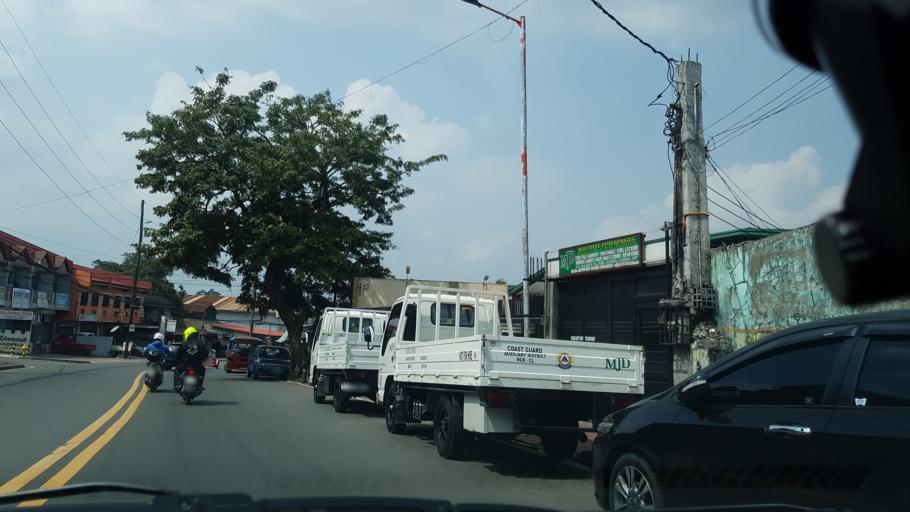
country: PH
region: Calabarzon
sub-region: Province of Rizal
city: Antipolo
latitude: 14.6608
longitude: 121.1187
